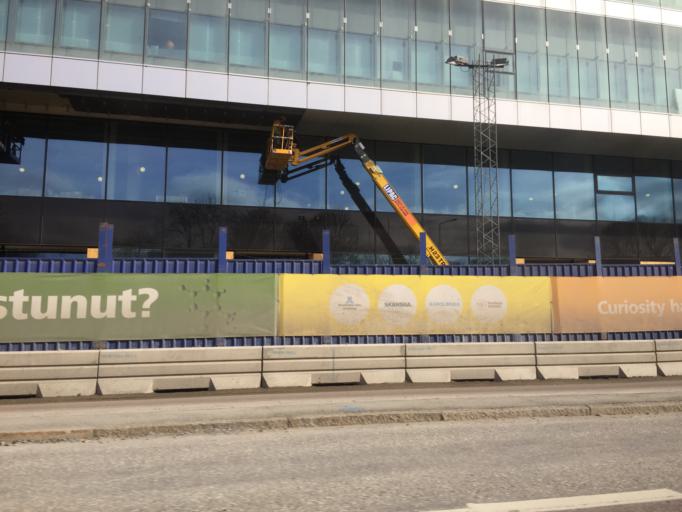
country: SE
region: Stockholm
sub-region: Solna Kommun
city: Solna
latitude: 59.3484
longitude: 18.0292
